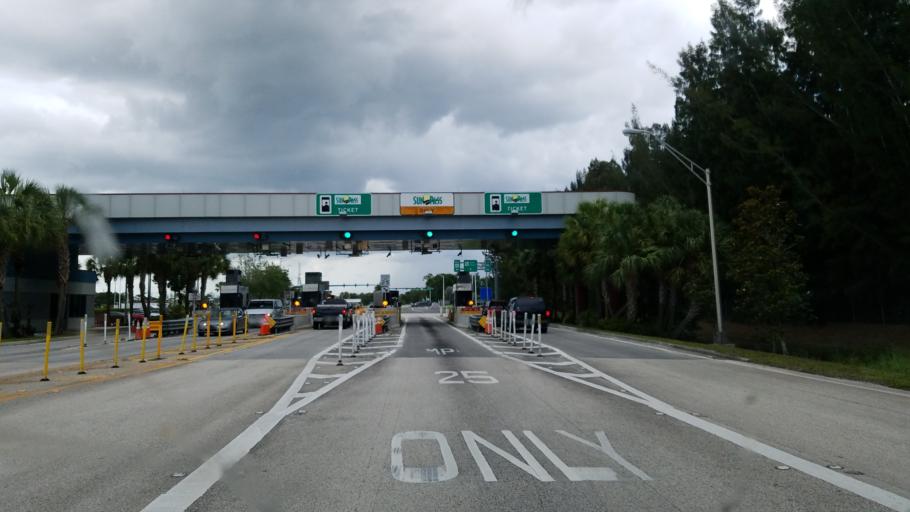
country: US
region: Florida
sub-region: Martin County
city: Palm City
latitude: 27.1595
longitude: -80.3006
